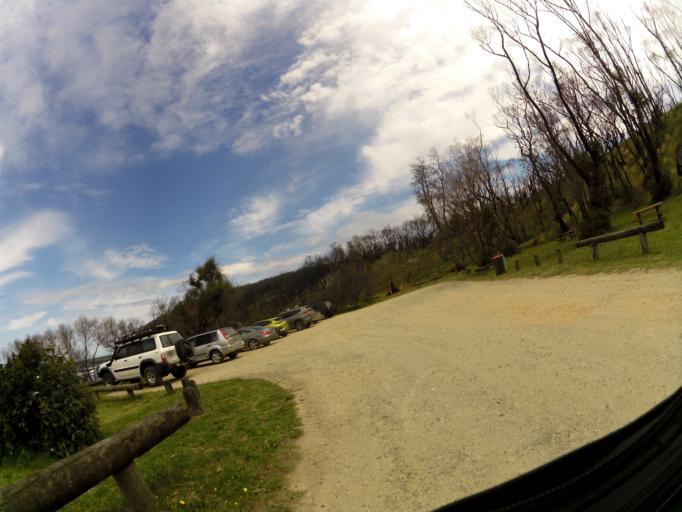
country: AU
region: Victoria
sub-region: East Gippsland
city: Lakes Entrance
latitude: -37.8024
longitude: 148.7412
